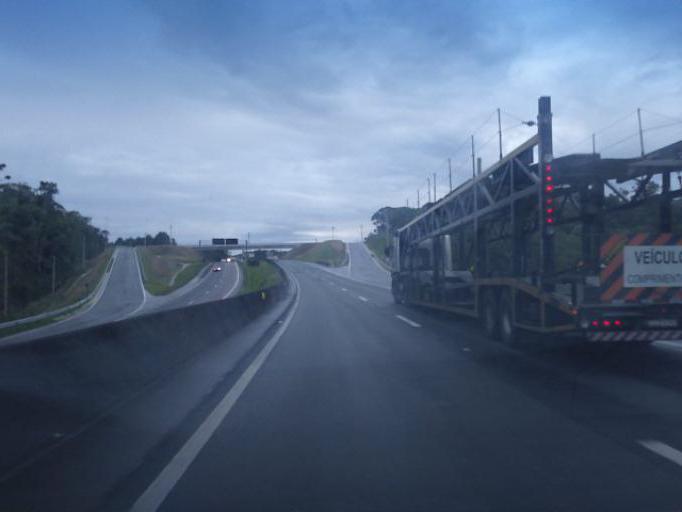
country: BR
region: Parana
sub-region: Sao Jose Dos Pinhais
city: Sao Jose dos Pinhais
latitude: -25.7663
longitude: -49.1242
